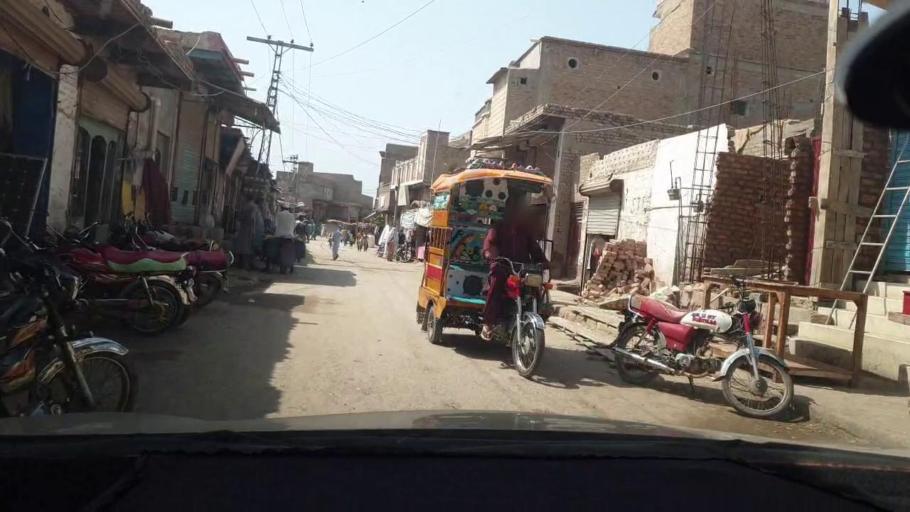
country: PK
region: Sindh
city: Kambar
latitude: 27.5876
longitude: 68.0020
